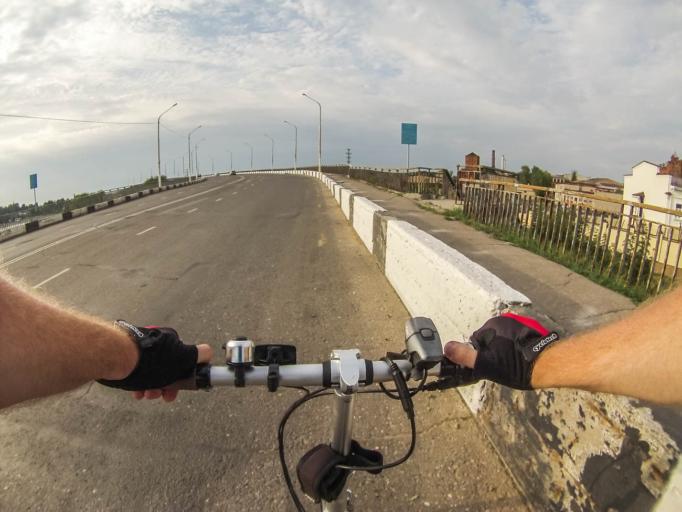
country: RU
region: Kostroma
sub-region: Kostromskoy Rayon
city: Kostroma
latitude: 57.7777
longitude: 40.9034
